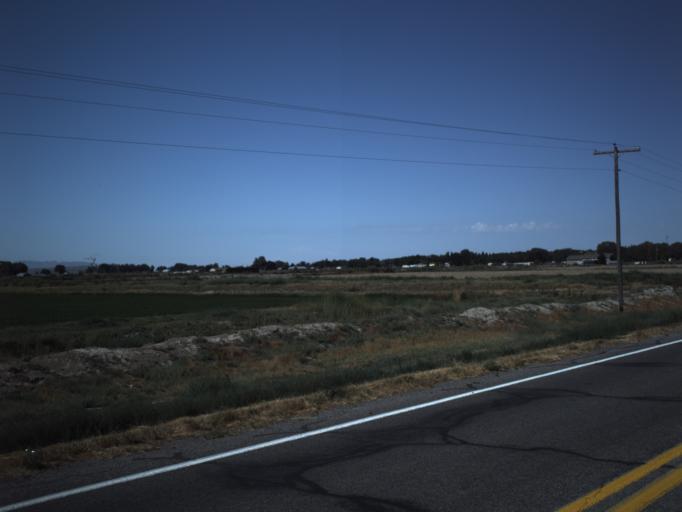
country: US
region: Utah
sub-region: Millard County
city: Delta
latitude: 39.3308
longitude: -112.6561
